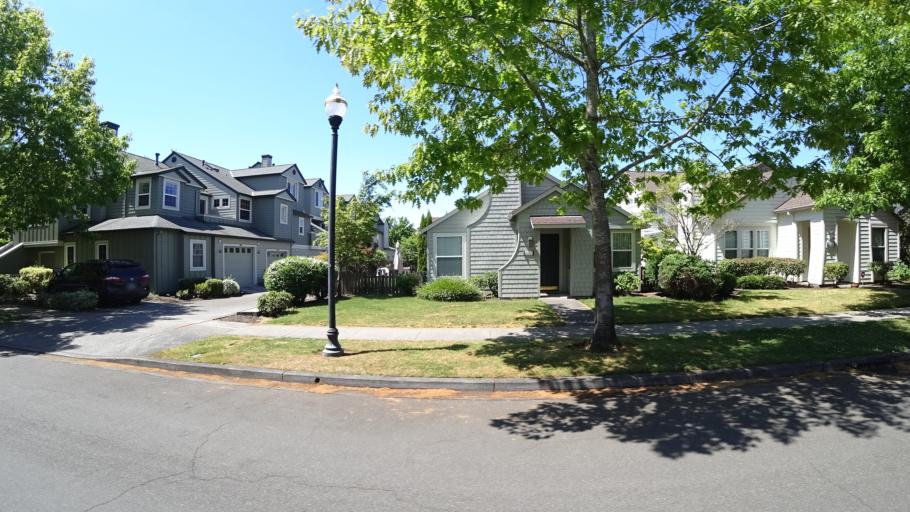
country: US
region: Oregon
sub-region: Washington County
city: Rockcreek
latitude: 45.5356
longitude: -122.9135
